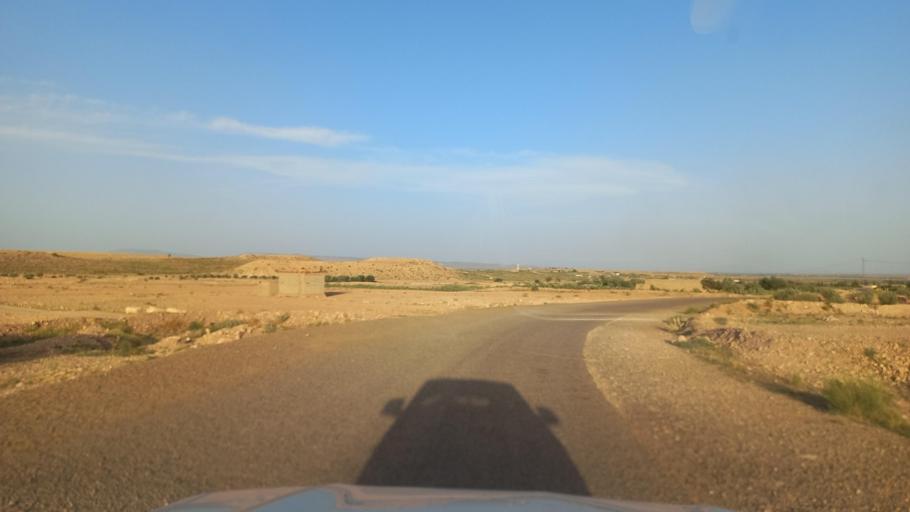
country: TN
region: Al Qasrayn
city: Kasserine
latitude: 35.2740
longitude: 8.9220
